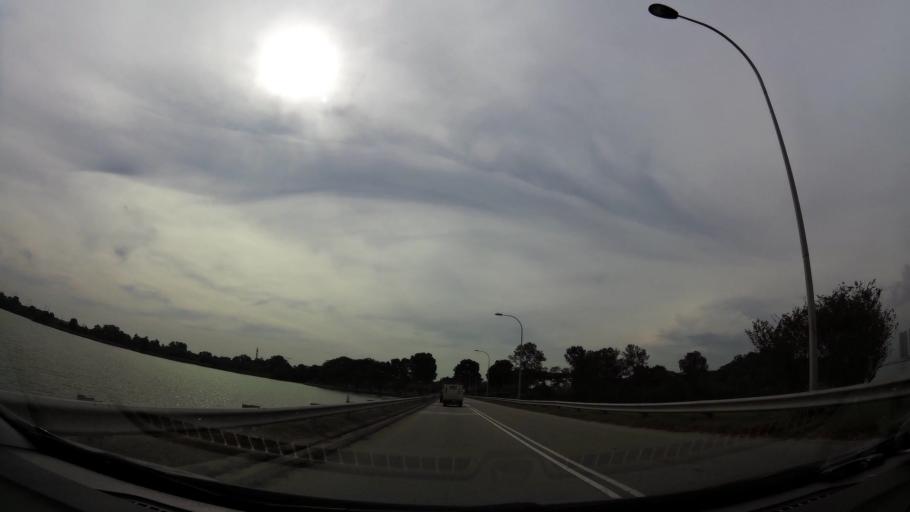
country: MY
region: Johor
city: Johor Bahru
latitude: 1.4386
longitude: 103.7400
